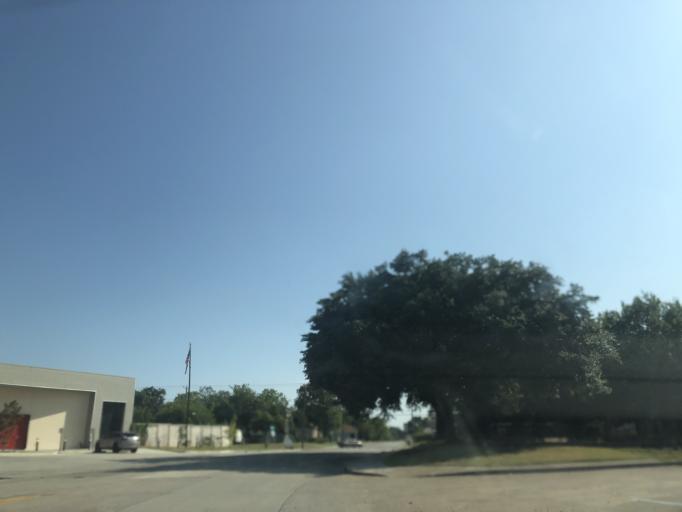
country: US
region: Texas
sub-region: Dallas County
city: Dallas
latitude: 32.7629
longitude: -96.7721
